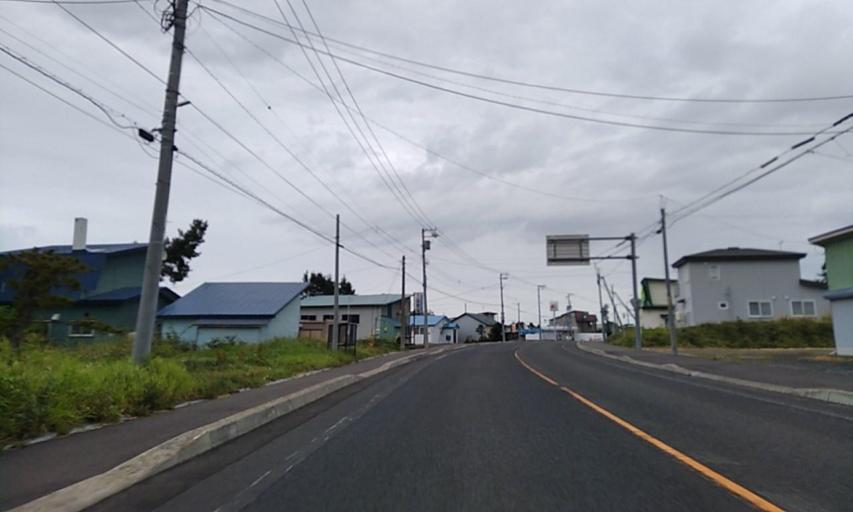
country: JP
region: Hokkaido
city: Mombetsu
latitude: 44.5183
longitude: 143.0601
